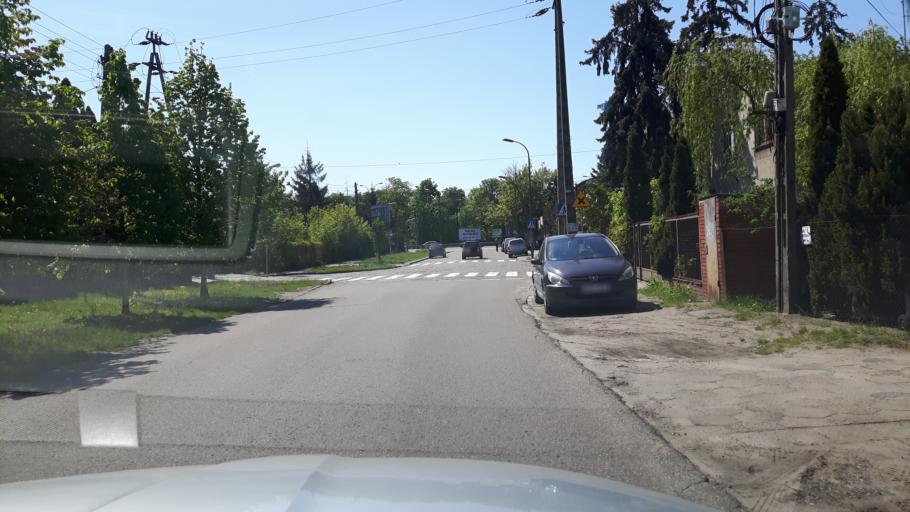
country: PL
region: Masovian Voivodeship
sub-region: Warszawa
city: Rembertow
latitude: 52.2274
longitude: 21.1540
